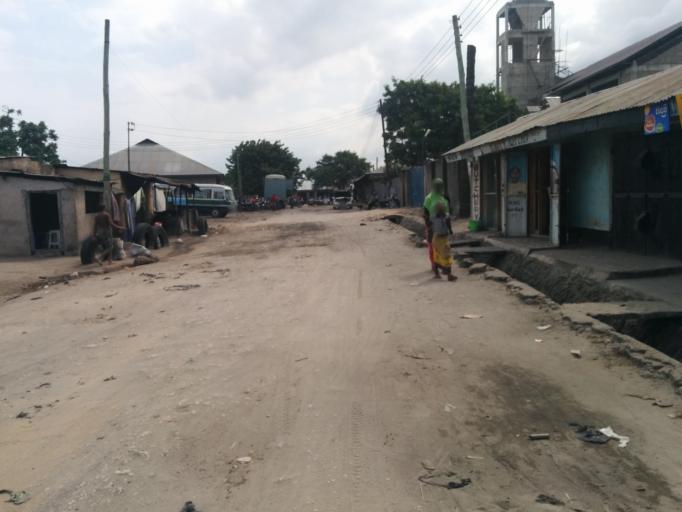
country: TZ
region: Dar es Salaam
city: Dar es Salaam
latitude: -6.8661
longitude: 39.2508
